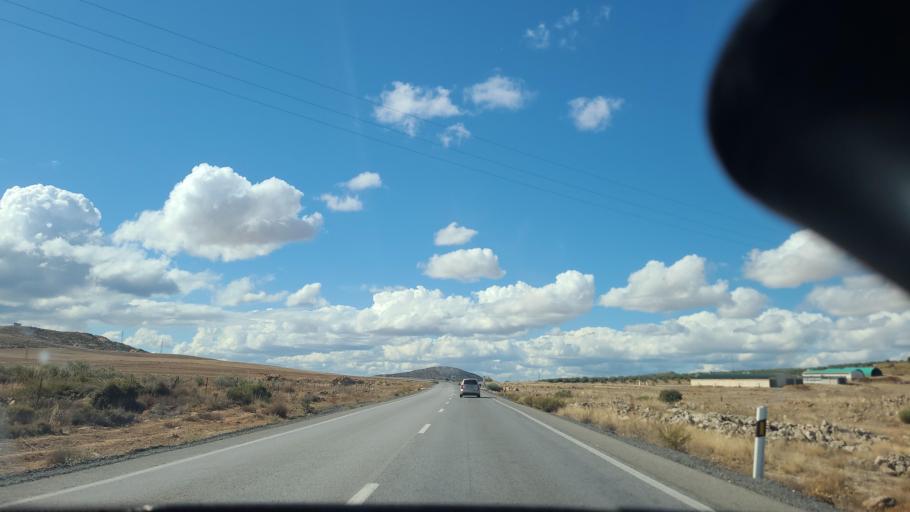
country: ES
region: Andalusia
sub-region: Provincia de Granada
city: Gobernador
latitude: 37.4119
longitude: -3.3553
